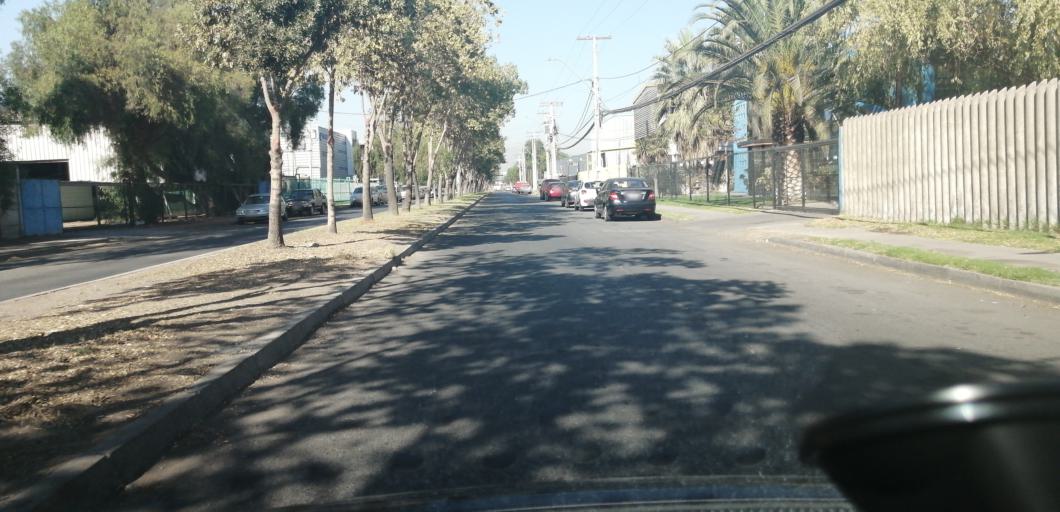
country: CL
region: Santiago Metropolitan
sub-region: Provincia de Santiago
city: Lo Prado
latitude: -33.3812
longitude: -70.7736
